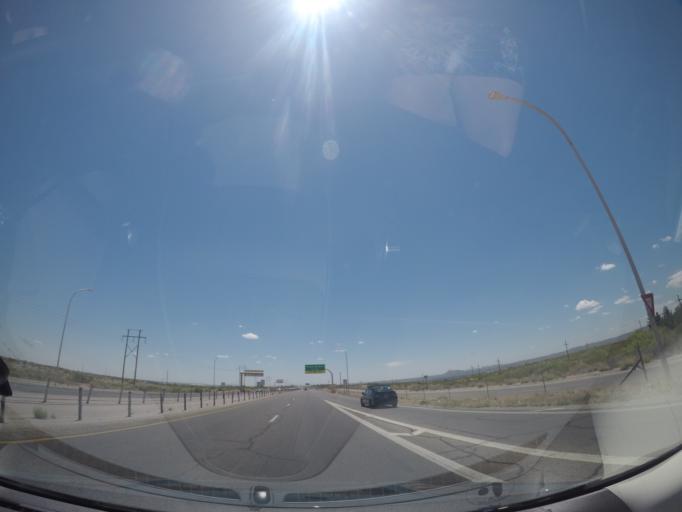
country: US
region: New Mexico
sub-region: Dona Ana County
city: Las Cruces
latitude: 32.3695
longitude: -106.7437
